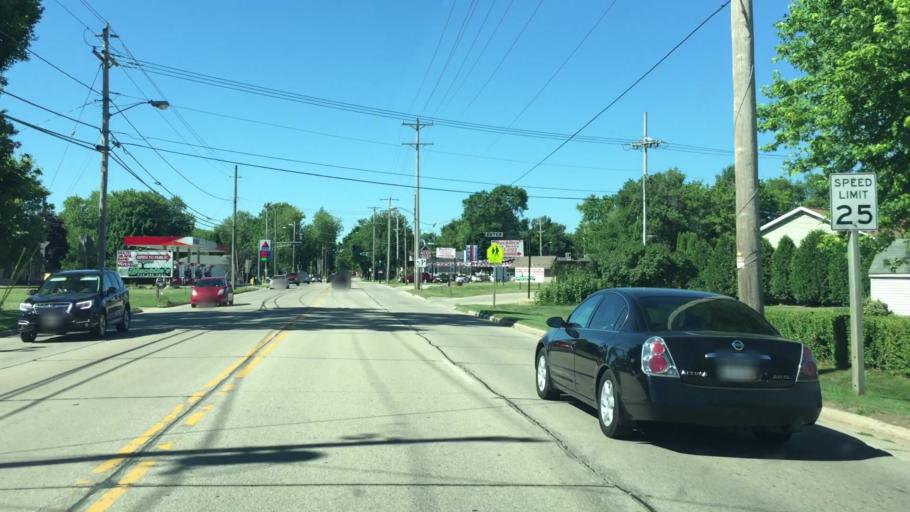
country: US
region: Wisconsin
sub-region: Winnebago County
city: Menasha
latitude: 44.2167
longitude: -88.4322
